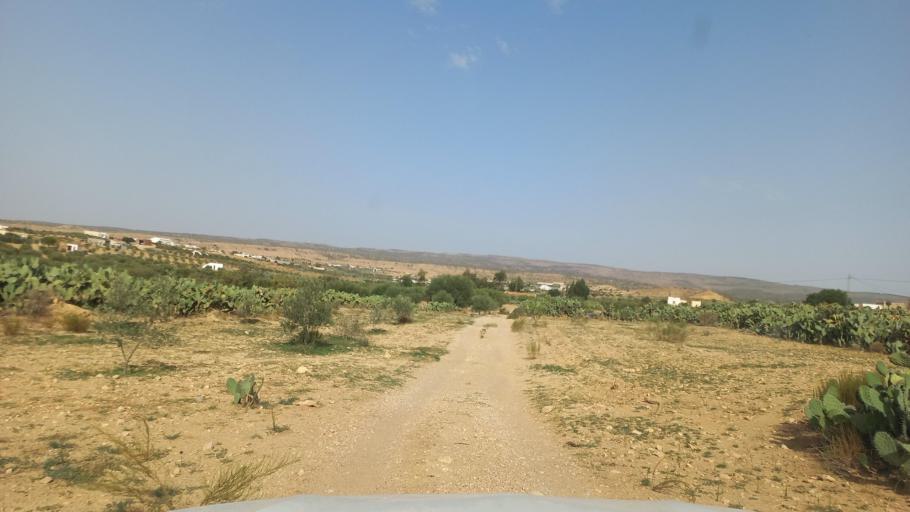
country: TN
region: Al Qasrayn
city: Kasserine
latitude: 35.2979
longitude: 8.9600
